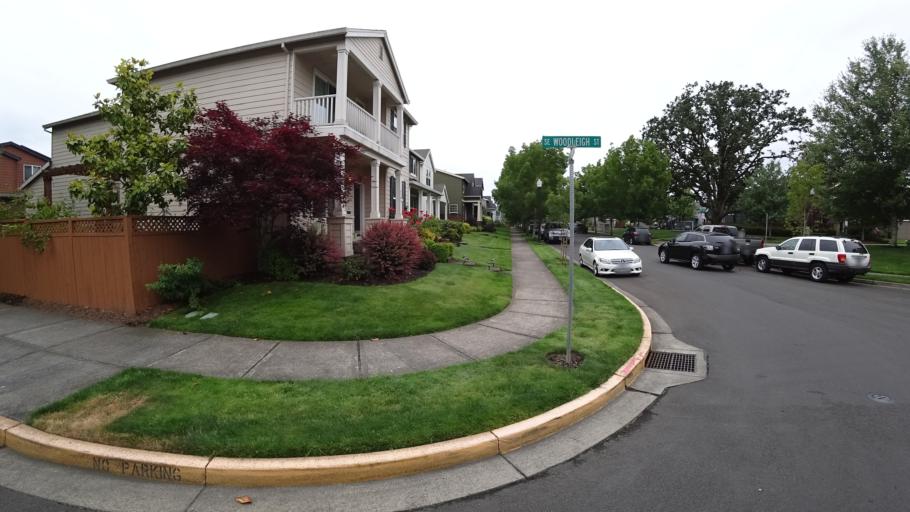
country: US
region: Oregon
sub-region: Washington County
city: Hillsboro
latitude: 45.4933
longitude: -122.9387
